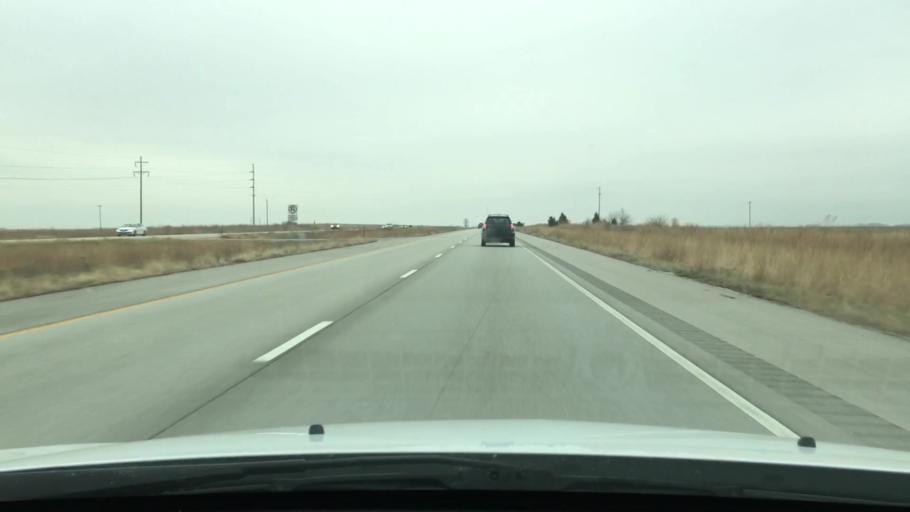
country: US
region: Illinois
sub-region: Morgan County
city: Jacksonville
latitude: 39.7379
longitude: -90.1152
